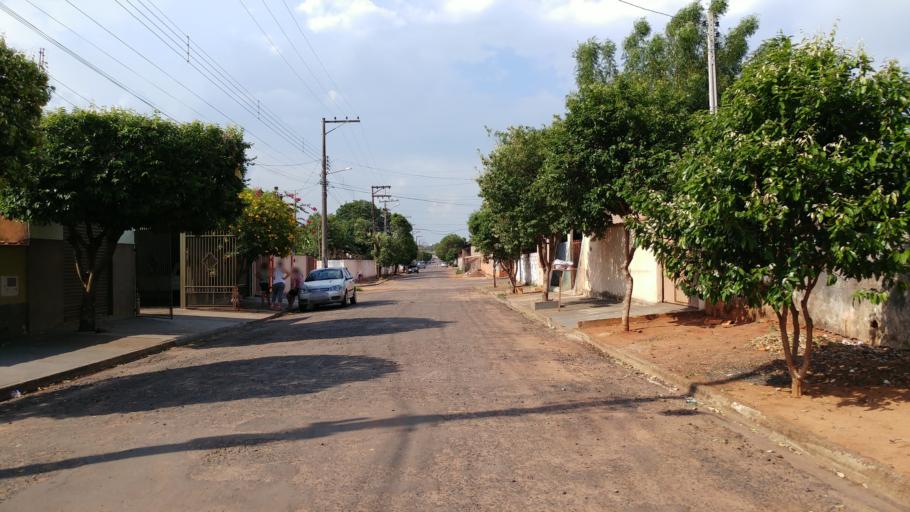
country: BR
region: Sao Paulo
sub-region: Paraguacu Paulista
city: Paraguacu Paulista
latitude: -22.4261
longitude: -50.5886
